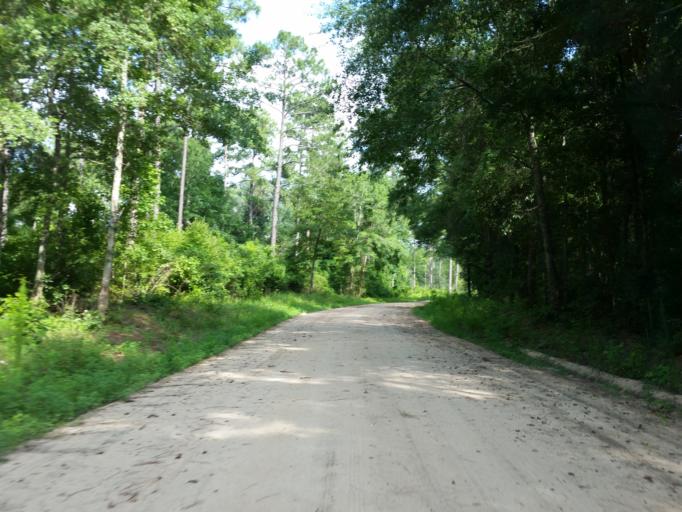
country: US
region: Georgia
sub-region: Lee County
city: Leesburg
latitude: 31.7641
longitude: -84.0206
